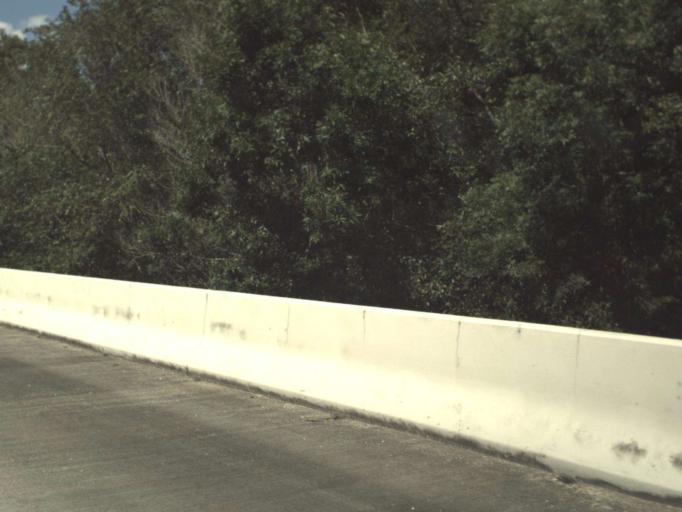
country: US
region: Florida
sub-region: Bay County
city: Laguna Beach
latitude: 30.4498
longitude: -85.8941
